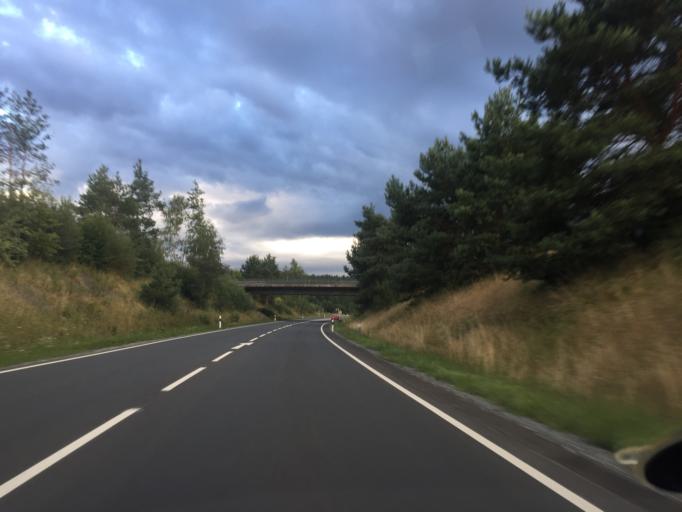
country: DE
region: Bavaria
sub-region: Upper Franconia
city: Seybothenreuth
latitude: 49.8952
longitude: 11.7127
